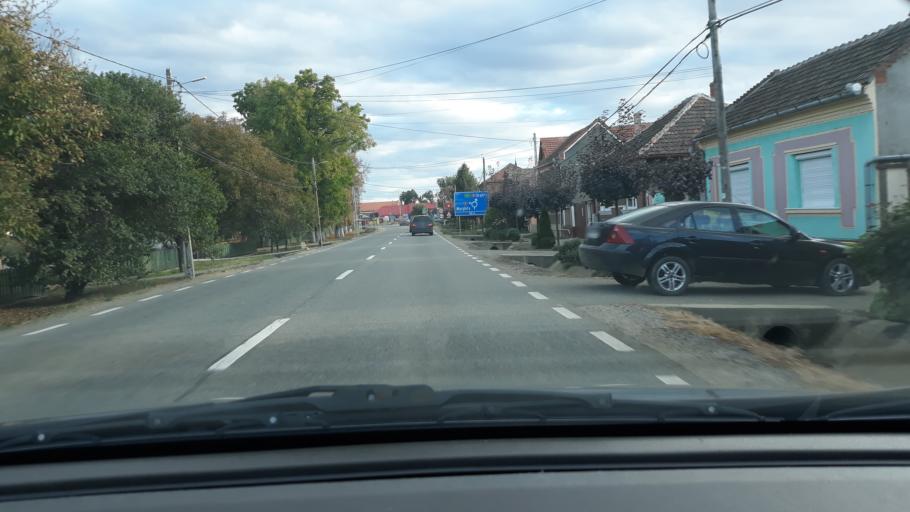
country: RO
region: Bihor
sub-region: Comuna Biharea
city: Biharea
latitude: 47.1589
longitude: 21.9222
